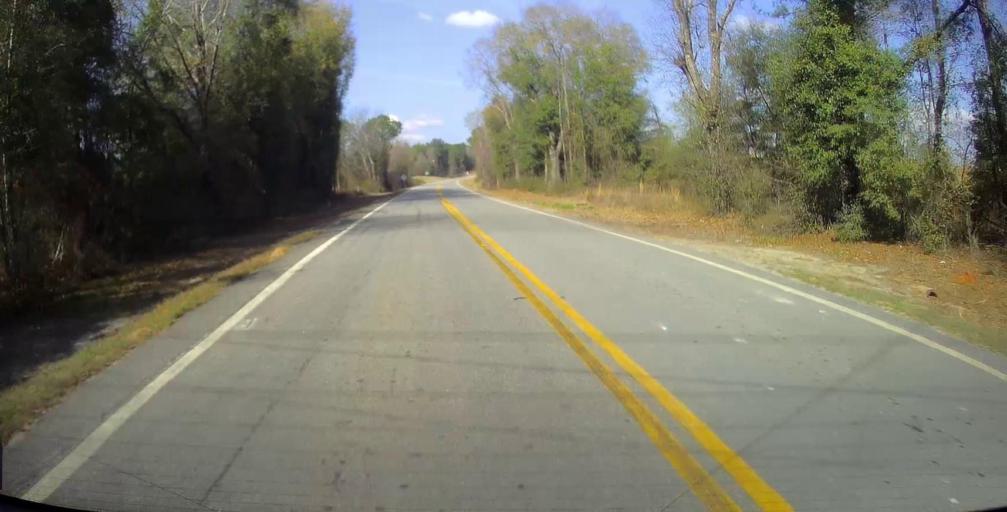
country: US
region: Georgia
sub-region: Twiggs County
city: Jeffersonville
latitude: 32.7756
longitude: -83.3330
